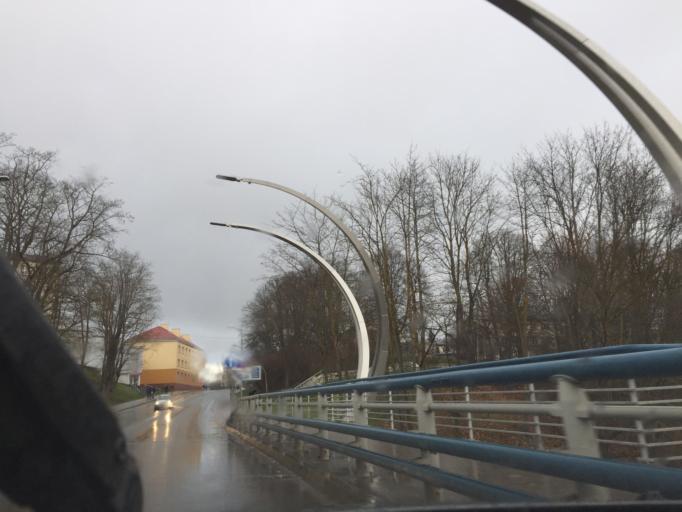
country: LV
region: Valmieras Rajons
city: Valmiera
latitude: 57.5362
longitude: 25.4240
